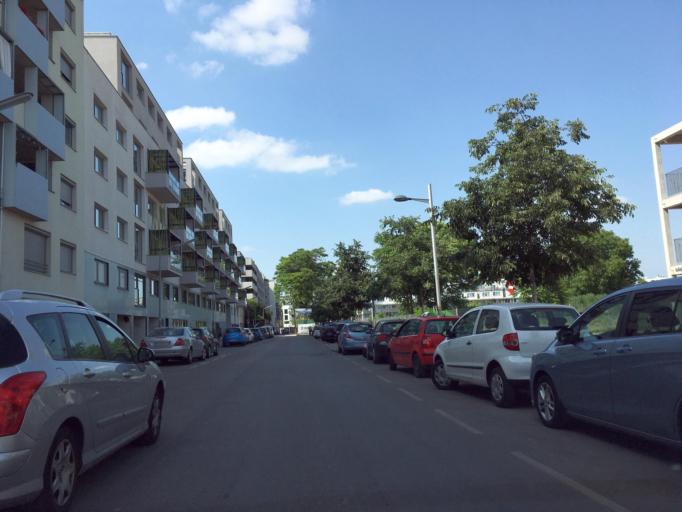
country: AT
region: Lower Austria
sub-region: Politischer Bezirk Wien-Umgebung
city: Gerasdorf bei Wien
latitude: 48.2483
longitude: 16.4343
